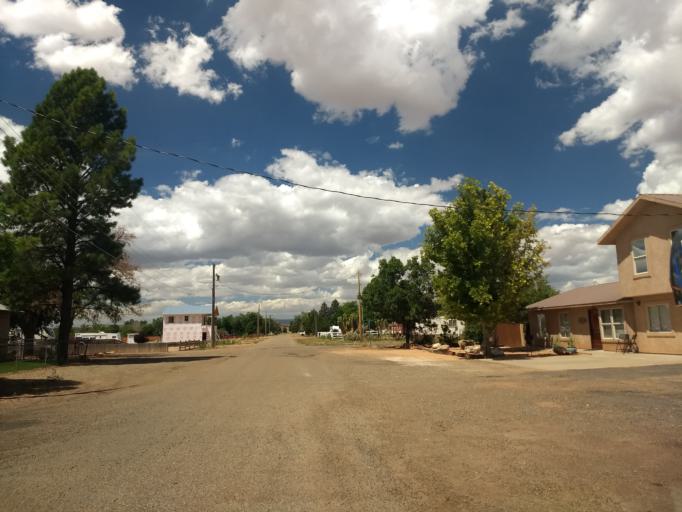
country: US
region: Arizona
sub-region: Coconino County
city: Fredonia
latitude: 36.9474
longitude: -112.5188
